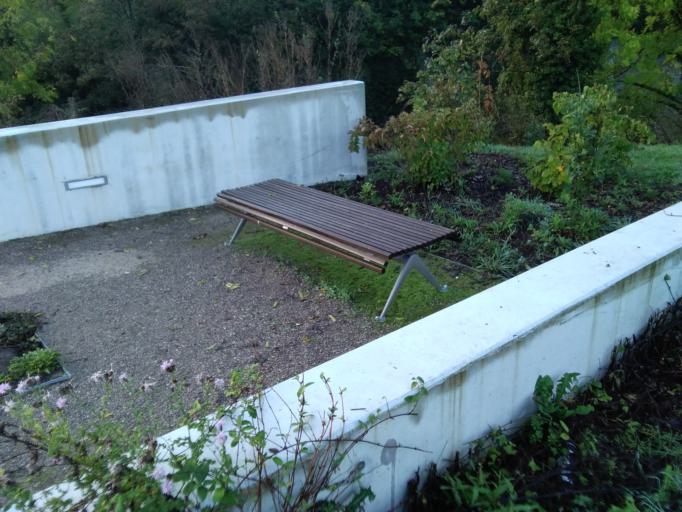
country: FR
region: Picardie
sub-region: Departement de la Somme
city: Amiens
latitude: 49.9057
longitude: 2.2967
